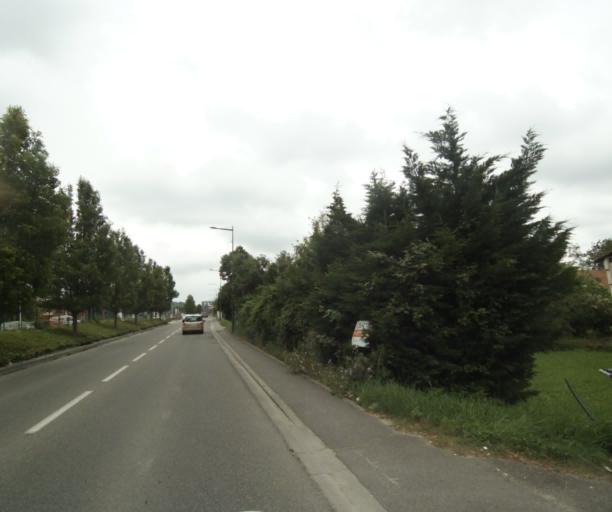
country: FR
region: Midi-Pyrenees
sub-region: Departement du Tarn-et-Garonne
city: Montauban
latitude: 44.0080
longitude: 1.3562
